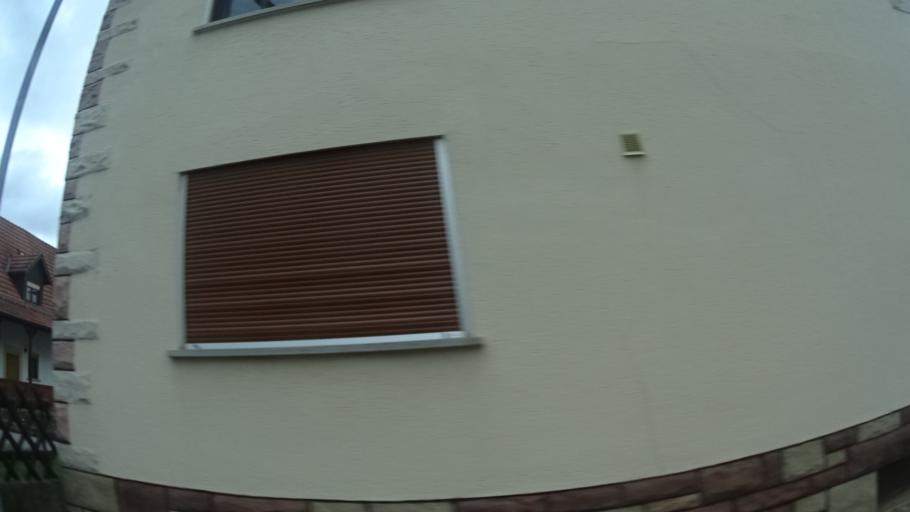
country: DE
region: Bavaria
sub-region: Regierungsbezirk Unterfranken
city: Hohenroth
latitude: 50.3374
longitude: 10.1401
